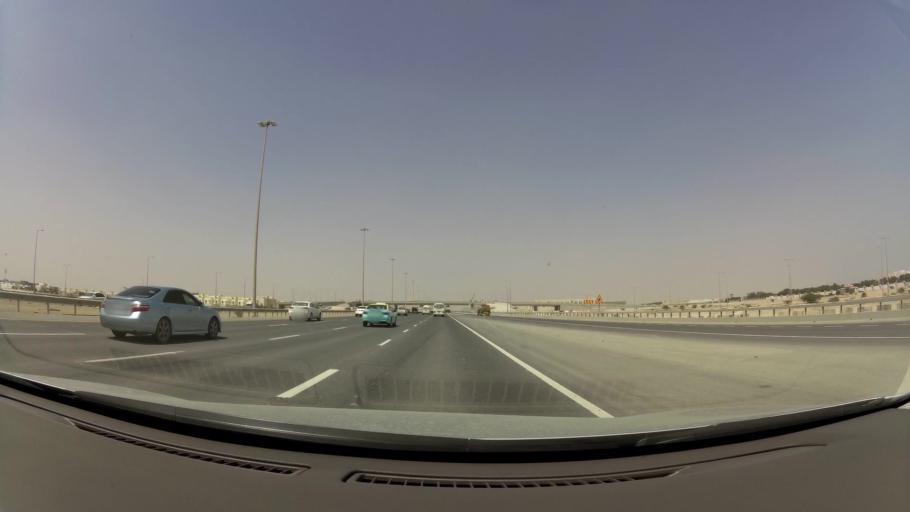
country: QA
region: Baladiyat Umm Salal
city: Umm Salal Muhammad
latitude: 25.4071
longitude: 51.4267
